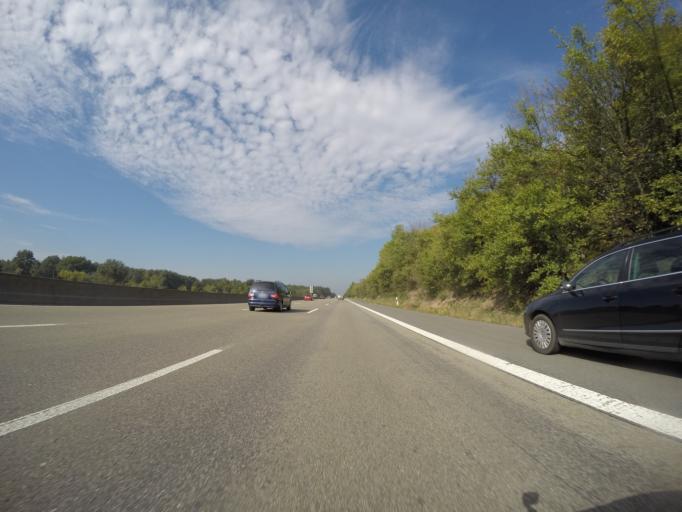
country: DE
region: Hesse
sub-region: Regierungsbezirk Darmstadt
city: Seligenstadt
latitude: 50.0090
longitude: 8.9786
